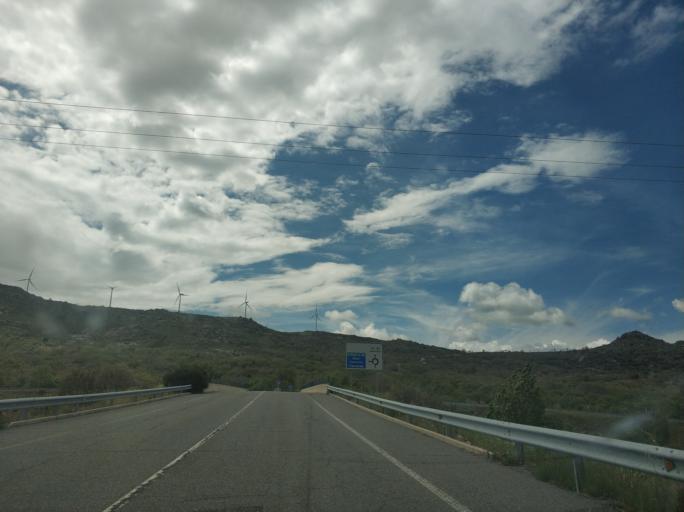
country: ES
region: Castille and Leon
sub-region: Provincia de Salamanca
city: Sorihuela
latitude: 40.4505
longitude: -5.6823
